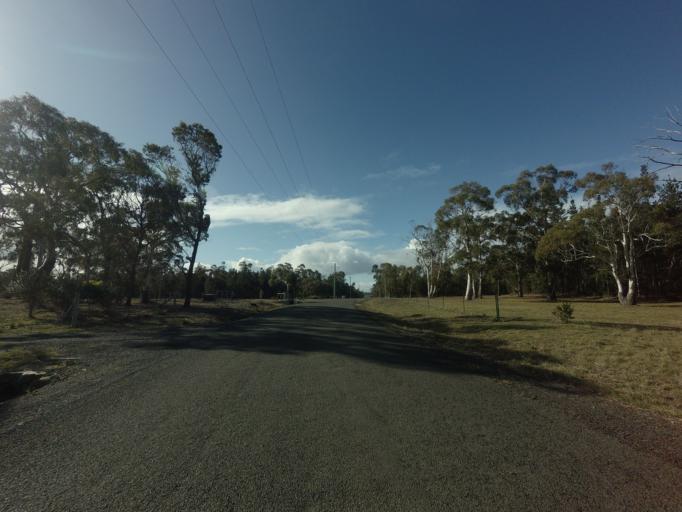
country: AU
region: Tasmania
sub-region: Sorell
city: Sorell
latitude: -42.3057
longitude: 147.9904
